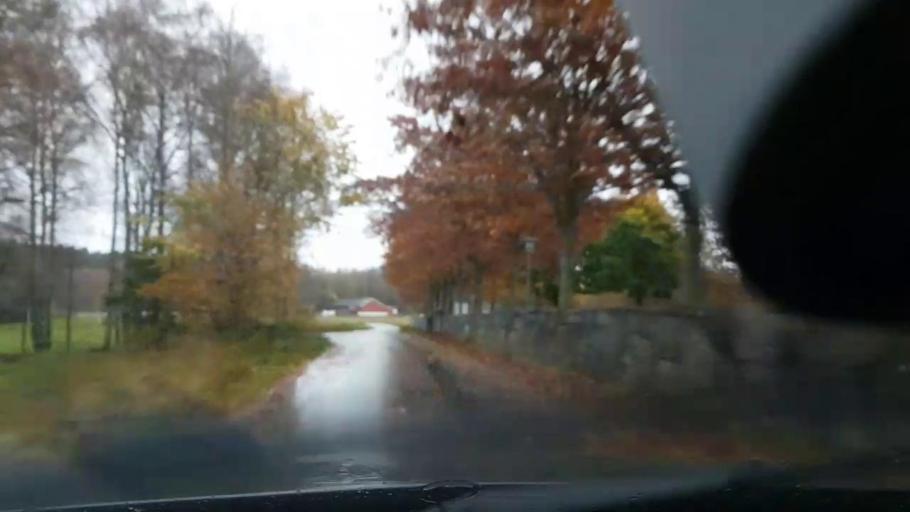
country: SE
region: Vaestra Goetaland
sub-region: Molndal
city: Lindome
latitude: 57.5794
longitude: 12.1083
